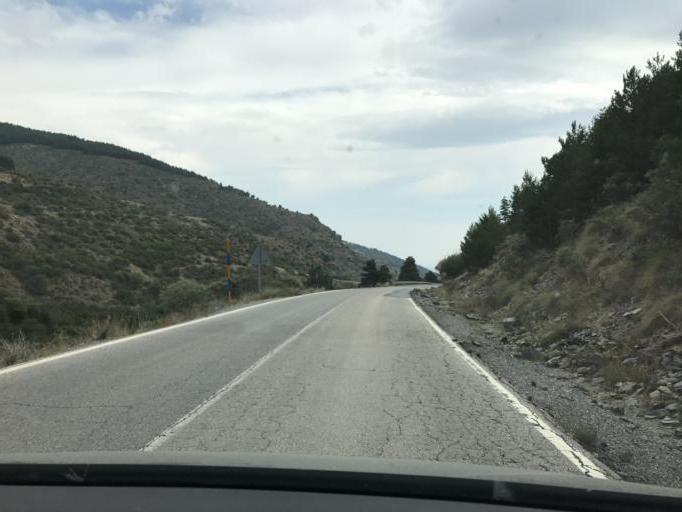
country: ES
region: Andalusia
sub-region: Provincia de Almeria
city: Bayarcal
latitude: 37.0839
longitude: -3.0235
